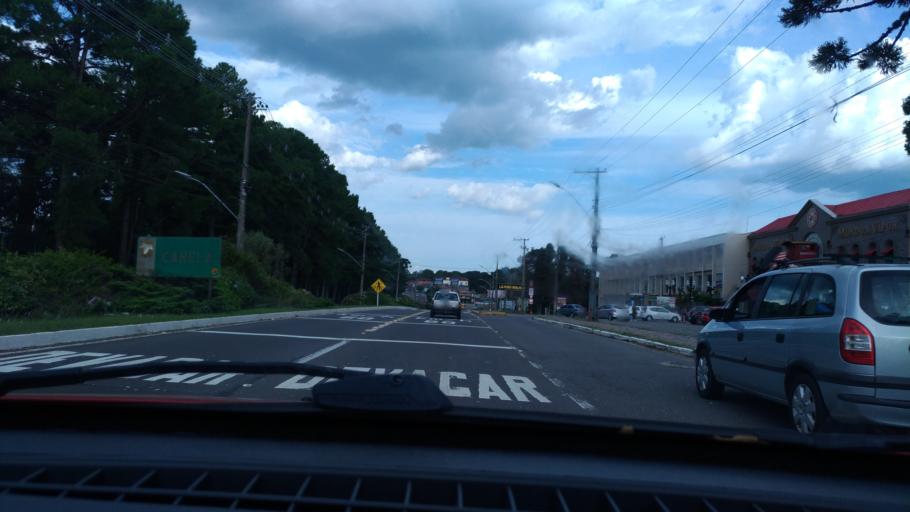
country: BR
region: Rio Grande do Sul
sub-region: Canela
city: Canela
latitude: -29.3607
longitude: -50.8365
